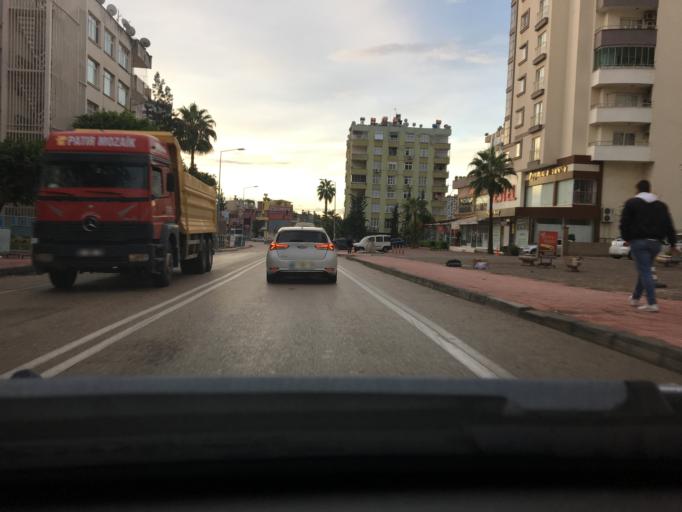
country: TR
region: Adana
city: Seyhan
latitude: 37.0242
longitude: 35.2917
